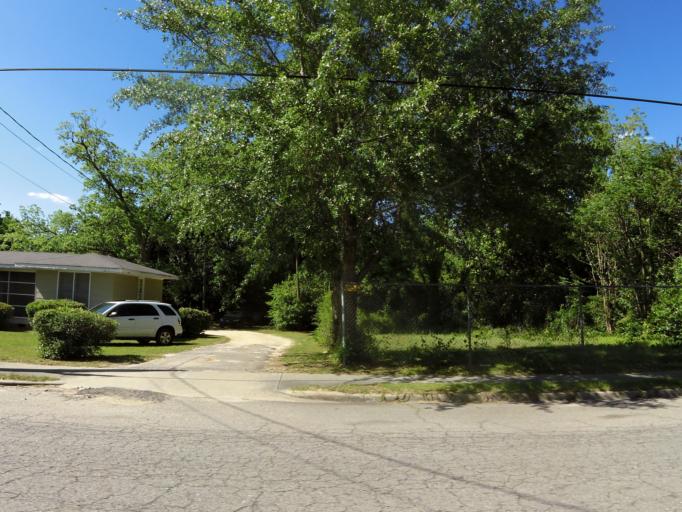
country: US
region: South Carolina
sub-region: Barnwell County
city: Blackville
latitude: 33.3535
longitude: -81.2688
